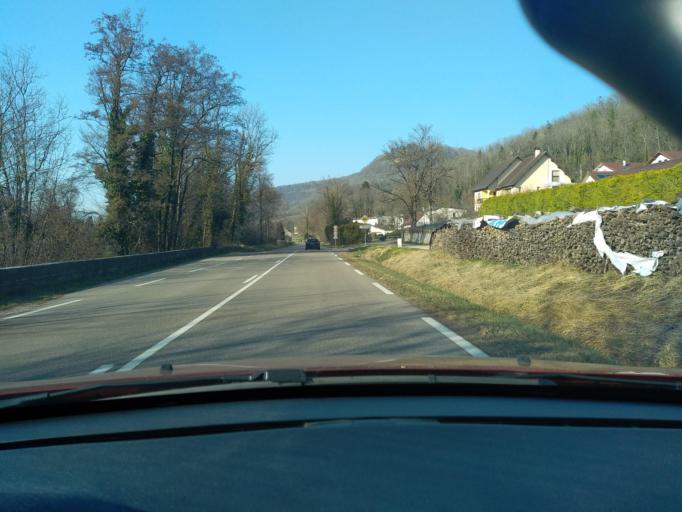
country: FR
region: Franche-Comte
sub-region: Departement du Jura
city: Perrigny
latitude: 46.6482
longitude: 5.6020
